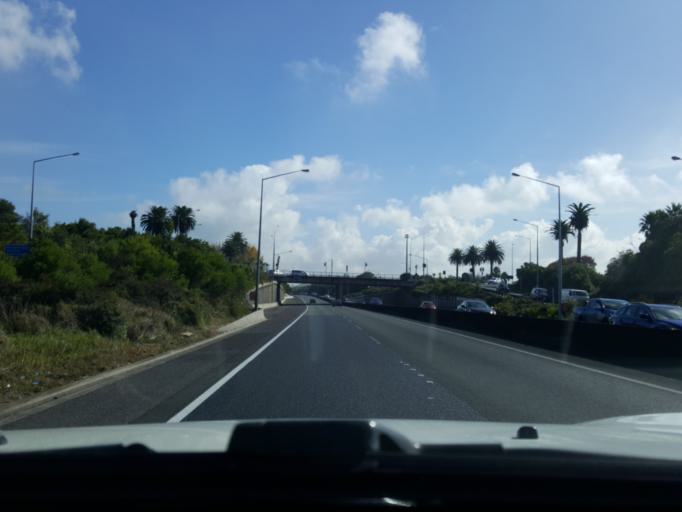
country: NZ
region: Auckland
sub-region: Auckland
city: Mangere
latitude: -36.9746
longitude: 174.8188
